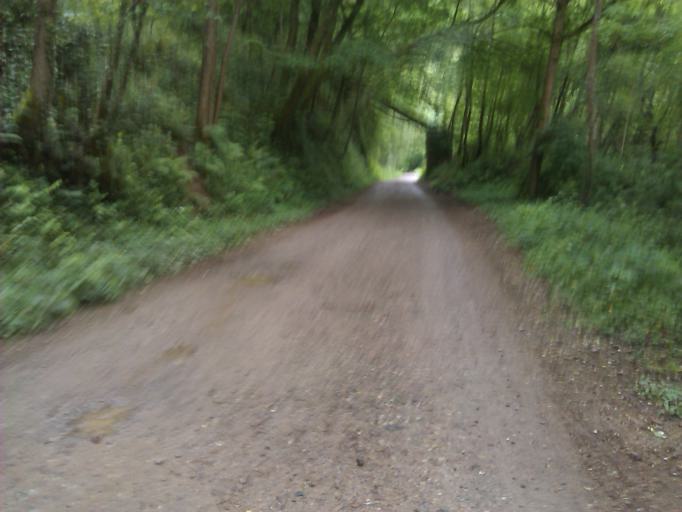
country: ES
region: Basque Country
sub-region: Provincia de Guipuzcoa
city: Andoain
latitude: 43.1855
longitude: -1.9954
